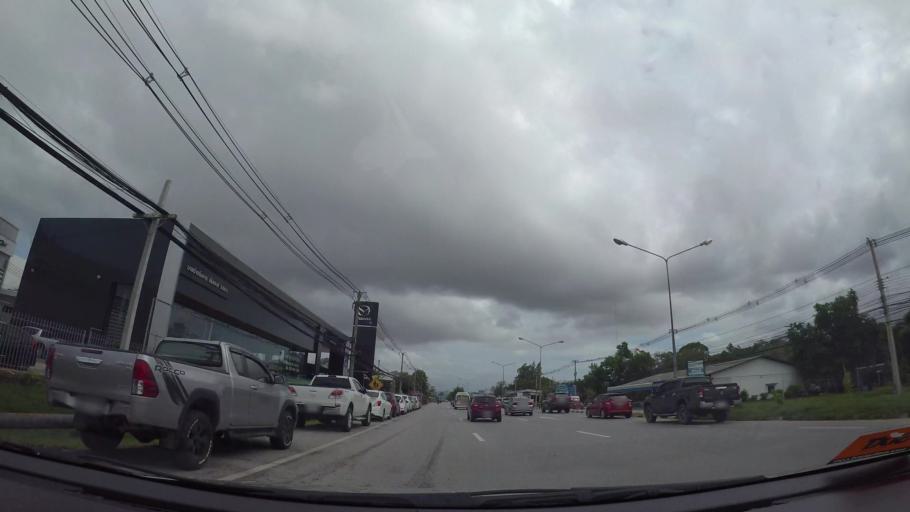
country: TH
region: Rayong
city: Rayong
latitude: 12.6857
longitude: 101.2149
